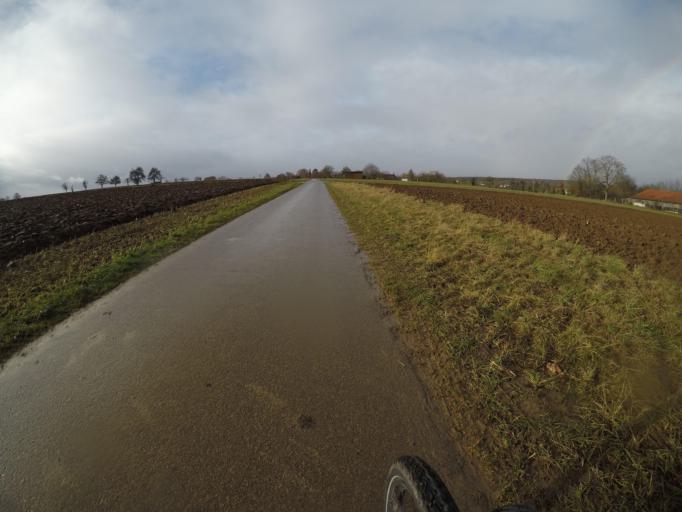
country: DE
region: Baden-Wuerttemberg
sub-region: Regierungsbezirk Stuttgart
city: Hemmingen
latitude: 48.8448
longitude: 9.0380
